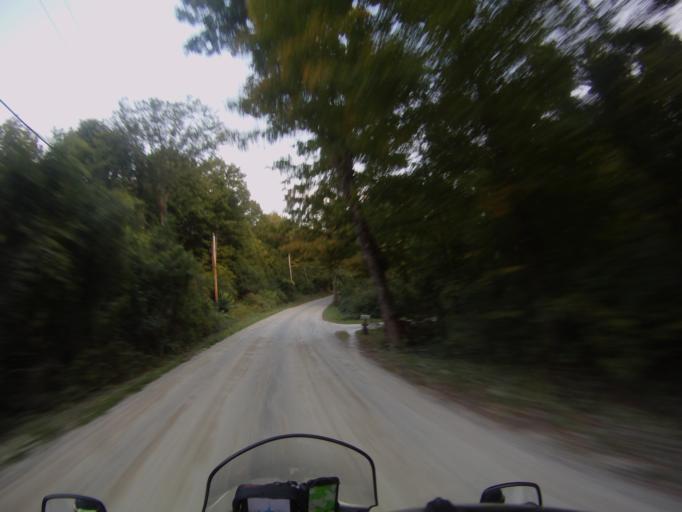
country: US
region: Vermont
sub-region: Rutland County
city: Brandon
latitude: 43.7830
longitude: -73.1369
